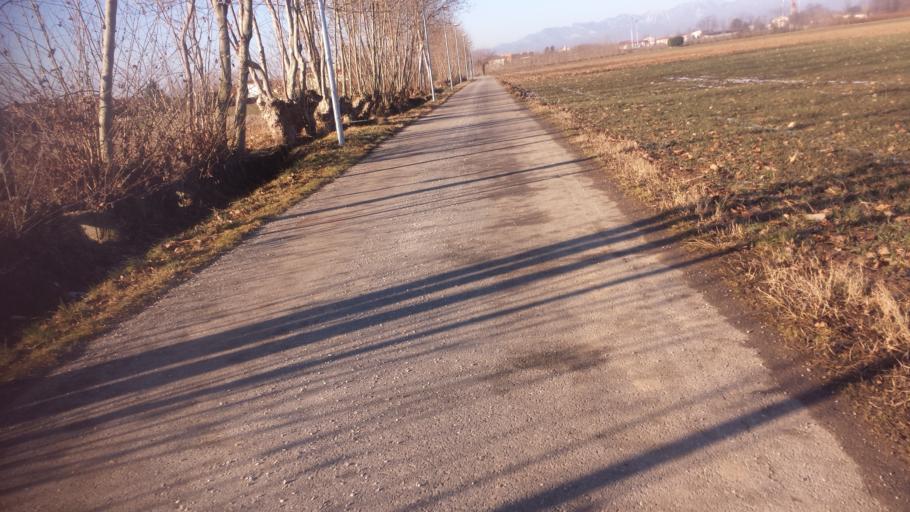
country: IT
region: Veneto
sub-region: Provincia di Vicenza
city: Tezze
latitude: 45.6852
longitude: 11.7164
